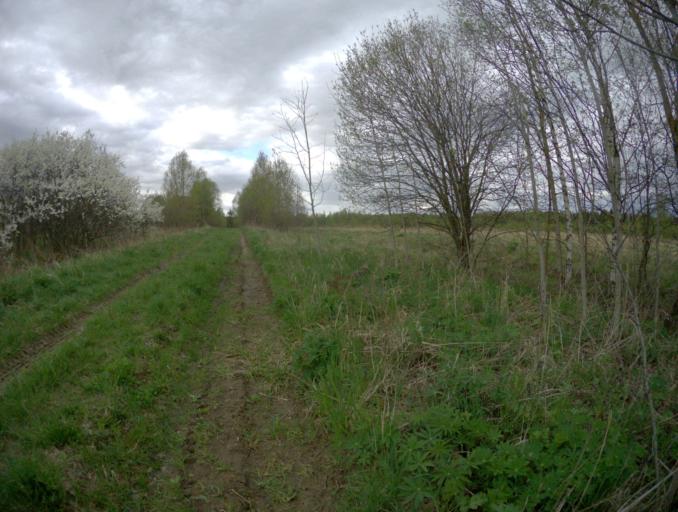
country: RU
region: Vladimir
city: Golovino
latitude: 55.9779
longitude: 40.4233
